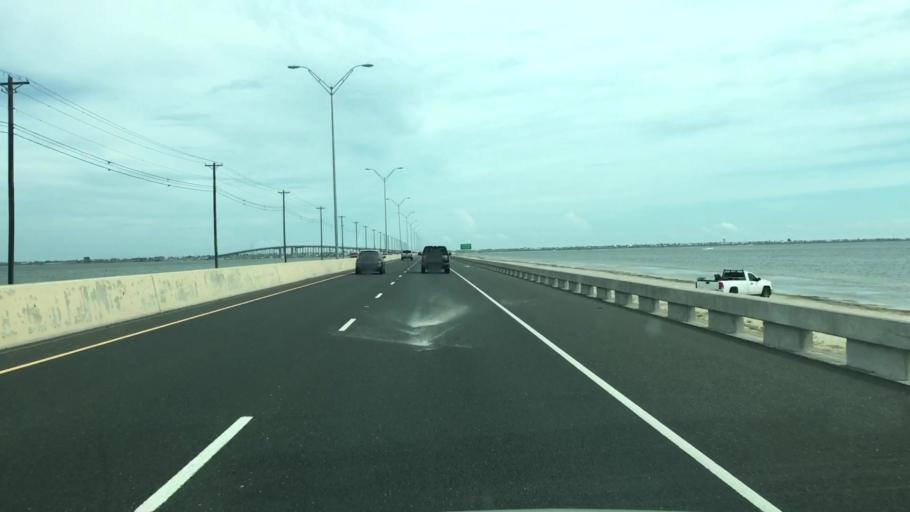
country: US
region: Texas
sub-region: Nueces County
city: Corpus Christi
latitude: 27.6487
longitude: -97.2527
